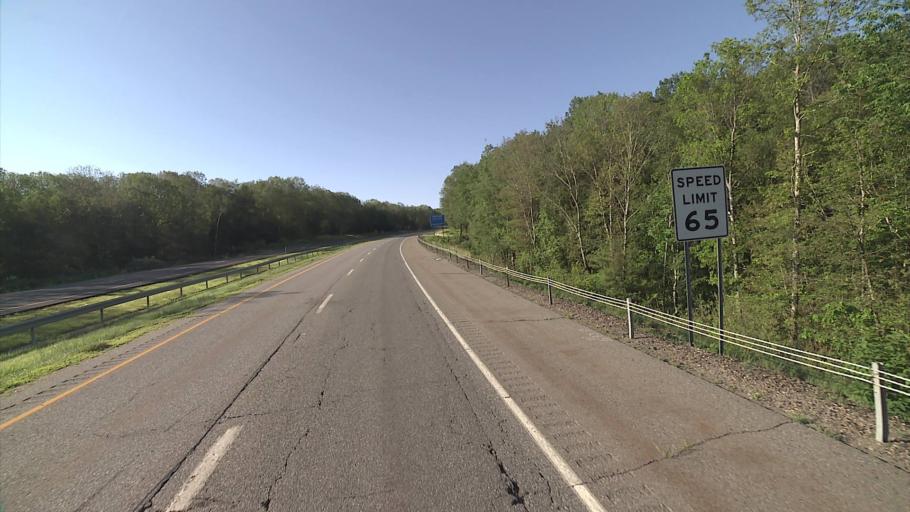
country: US
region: Connecticut
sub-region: Windham County
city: Danielson
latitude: 41.7854
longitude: -71.8725
